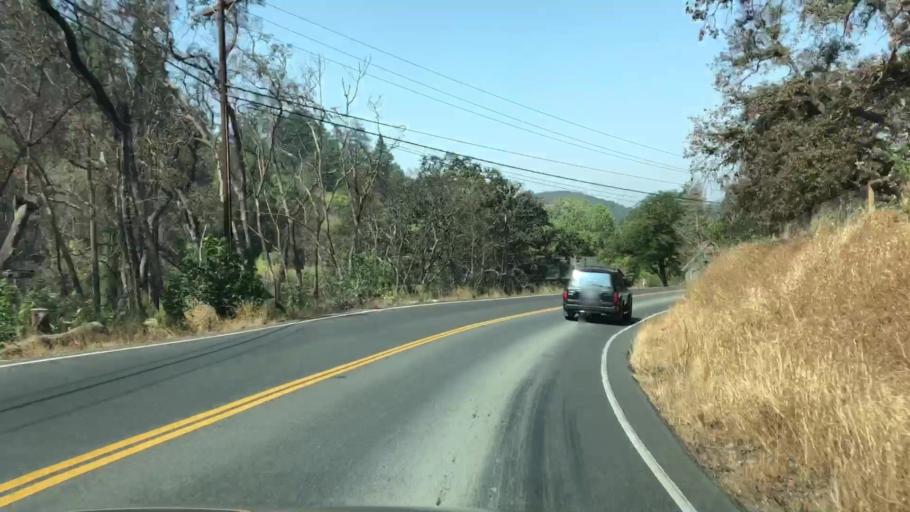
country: US
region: California
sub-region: Sonoma County
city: Larkfield-Wikiup
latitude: 38.5486
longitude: -122.7098
